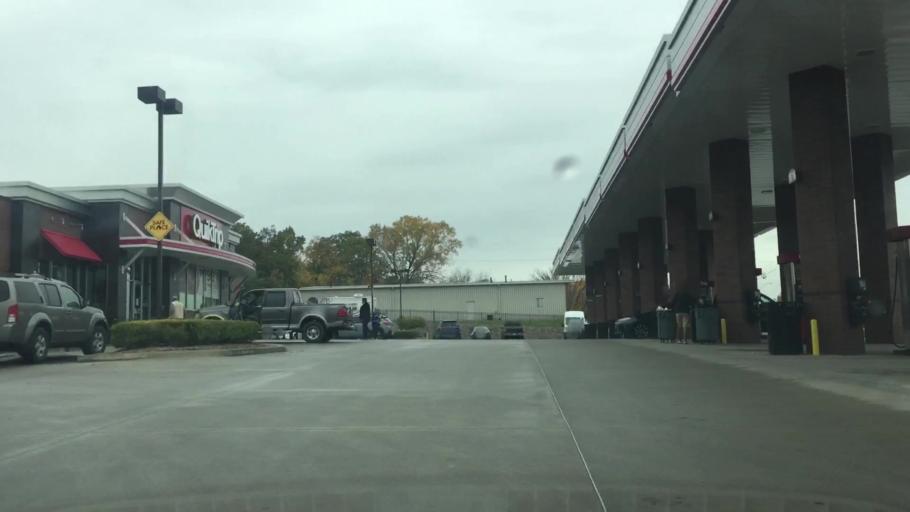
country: US
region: Kansas
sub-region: Wyandotte County
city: Edwardsville
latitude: 39.0086
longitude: -94.8238
